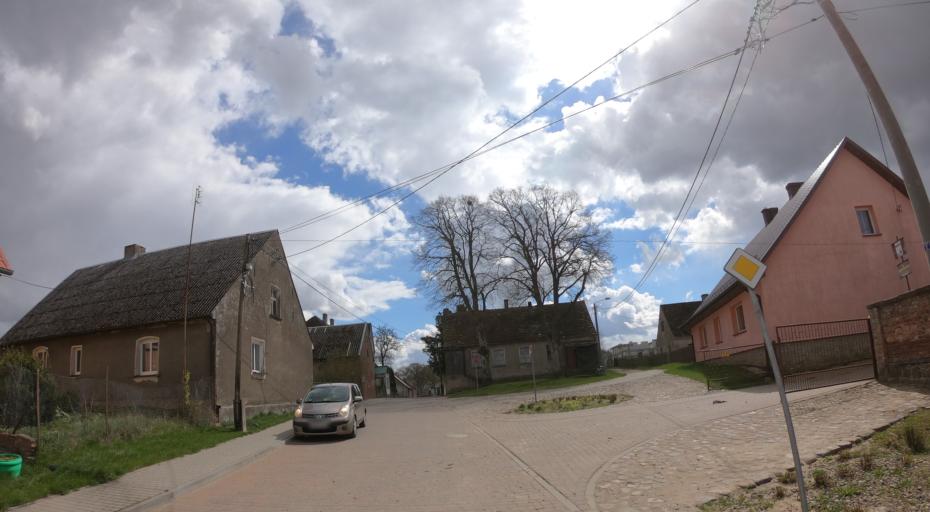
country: PL
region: West Pomeranian Voivodeship
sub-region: Powiat drawski
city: Drawsko Pomorskie
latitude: 53.5399
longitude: 15.8699
